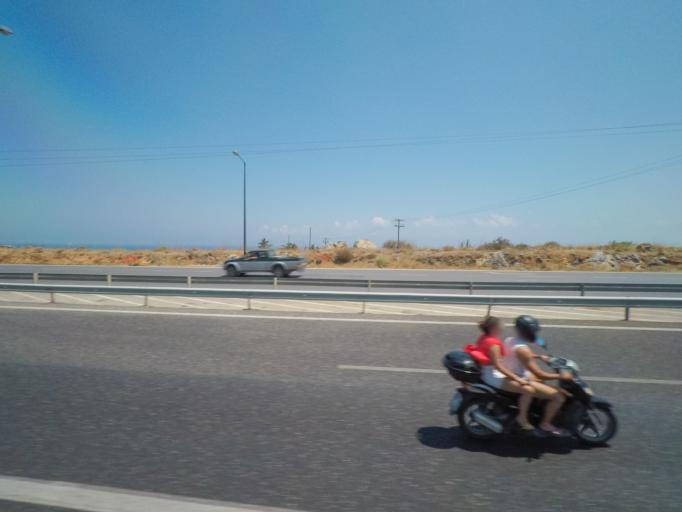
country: GR
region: Crete
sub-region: Nomos Irakleiou
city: Nea Alikarnassos
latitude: 35.3289
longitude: 25.1756
